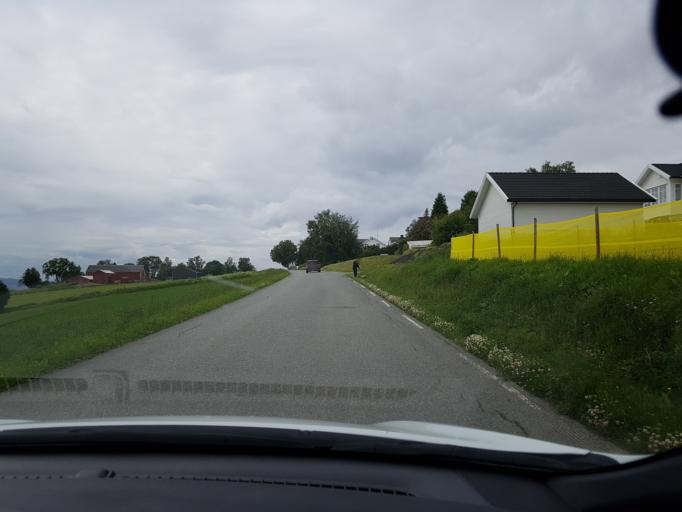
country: NO
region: Nord-Trondelag
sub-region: Frosta
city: Frosta
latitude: 63.5840
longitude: 10.7323
